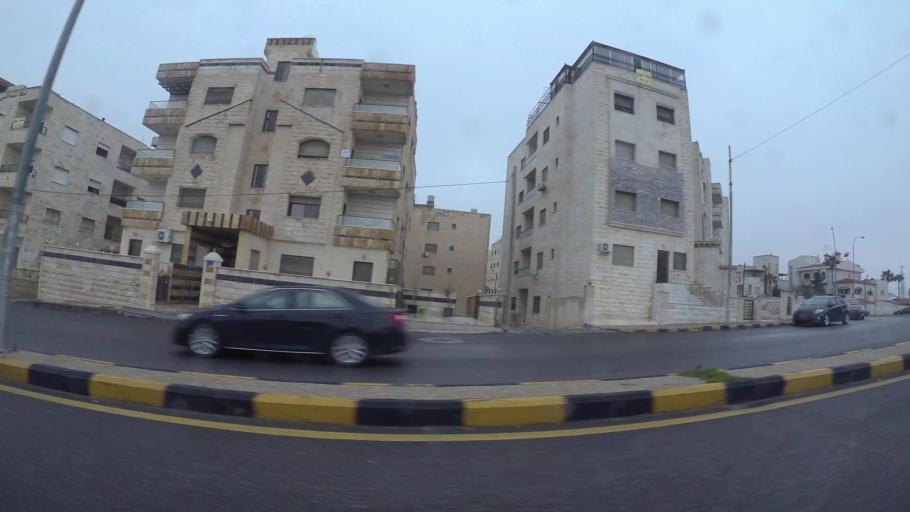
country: JO
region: Amman
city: Al Jubayhah
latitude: 32.0373
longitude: 35.8656
